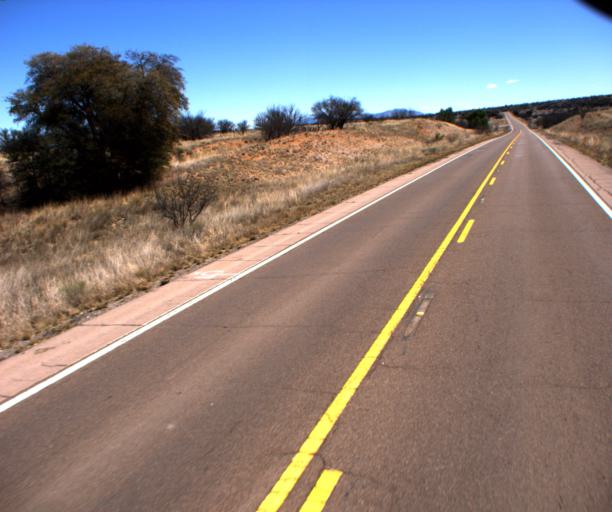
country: US
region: Arizona
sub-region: Pima County
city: Corona de Tucson
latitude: 31.6575
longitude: -110.7012
